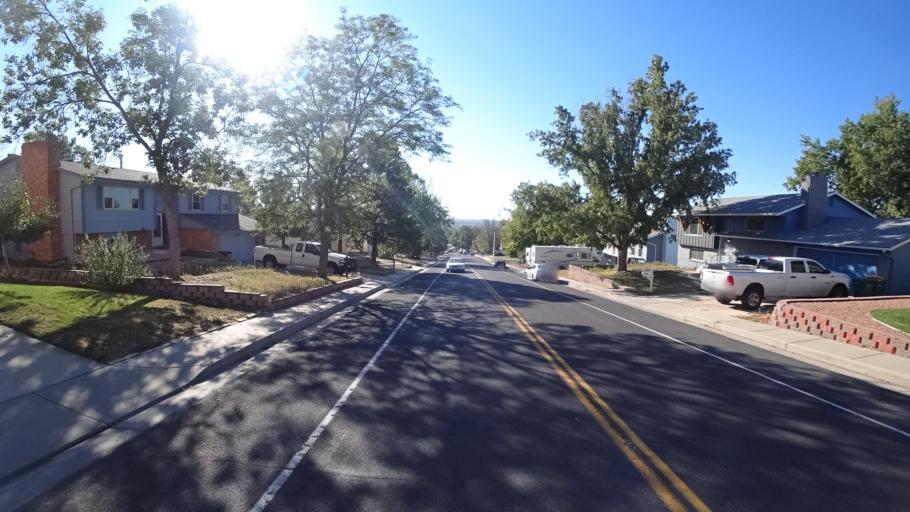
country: US
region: Colorado
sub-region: El Paso County
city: Cimarron Hills
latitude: 38.9097
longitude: -104.7646
